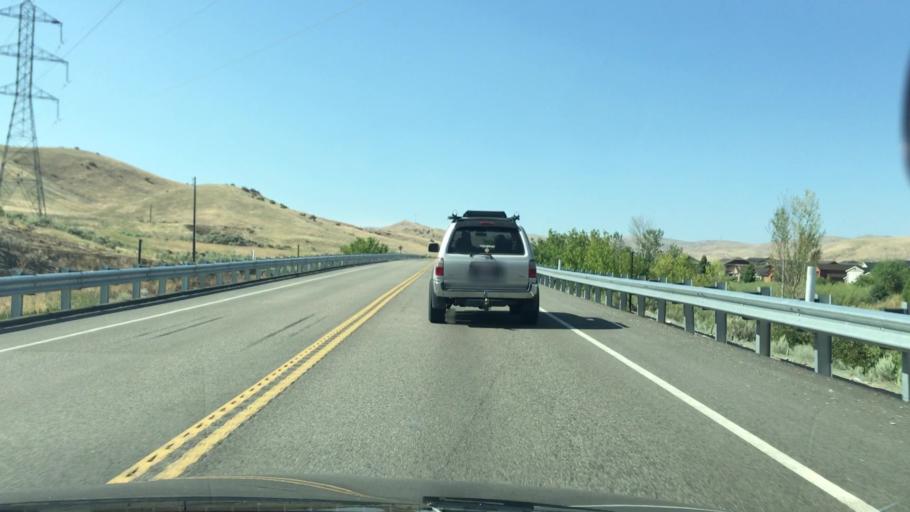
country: US
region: Idaho
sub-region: Ada County
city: Eagle
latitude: 43.7643
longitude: -116.2654
